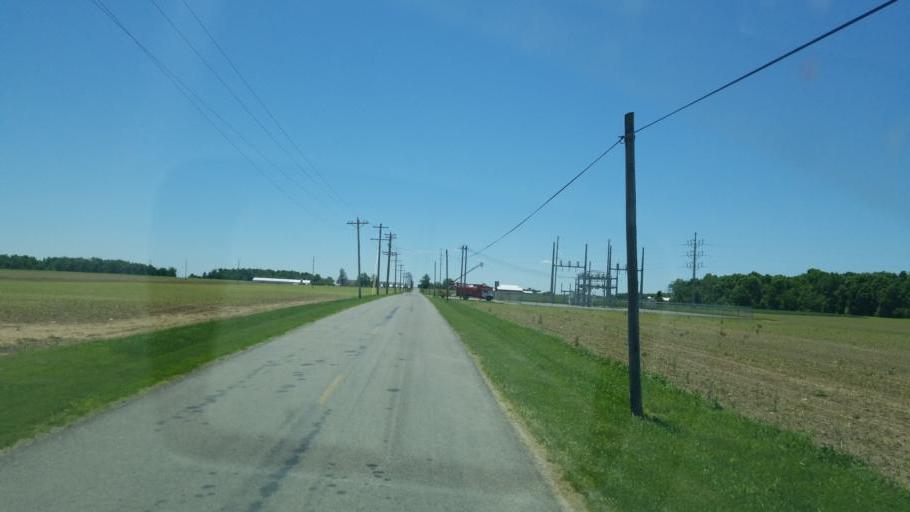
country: US
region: Ohio
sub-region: Mercer County
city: Fort Recovery
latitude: 40.3785
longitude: -84.7290
